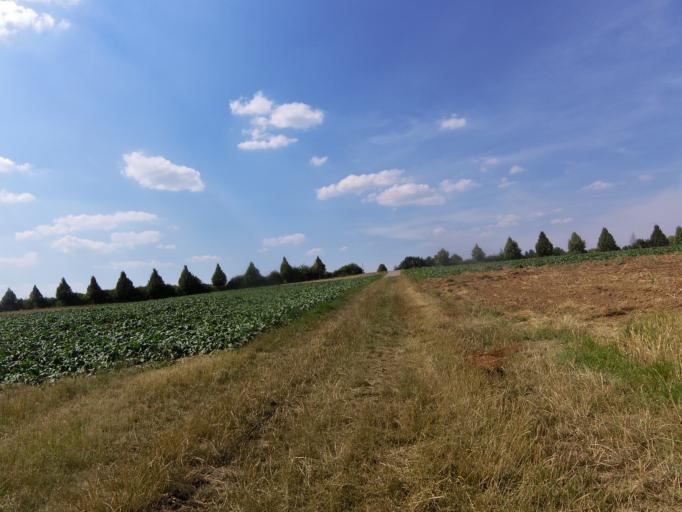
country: DE
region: Bavaria
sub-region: Regierungsbezirk Unterfranken
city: Estenfeld
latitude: 49.8202
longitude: 9.9940
